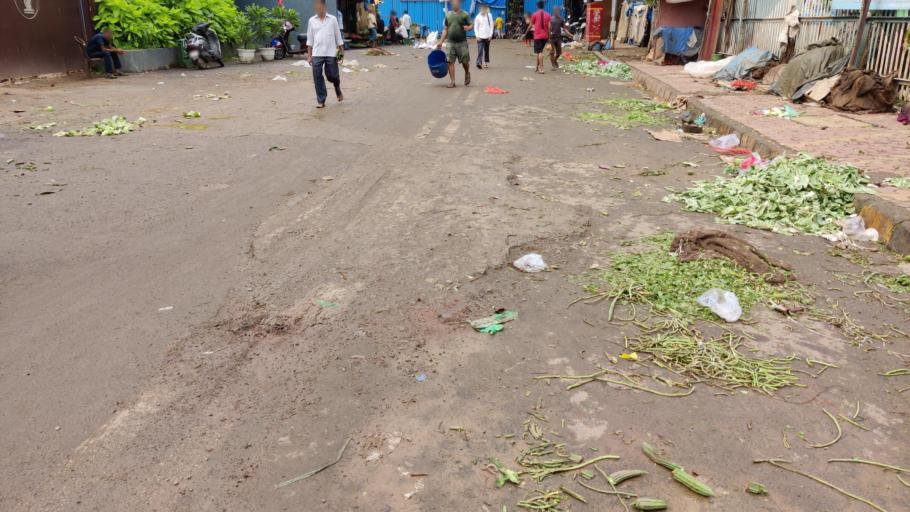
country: IN
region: Maharashtra
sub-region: Mumbai Suburban
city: Borivli
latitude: 19.2486
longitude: 72.8599
